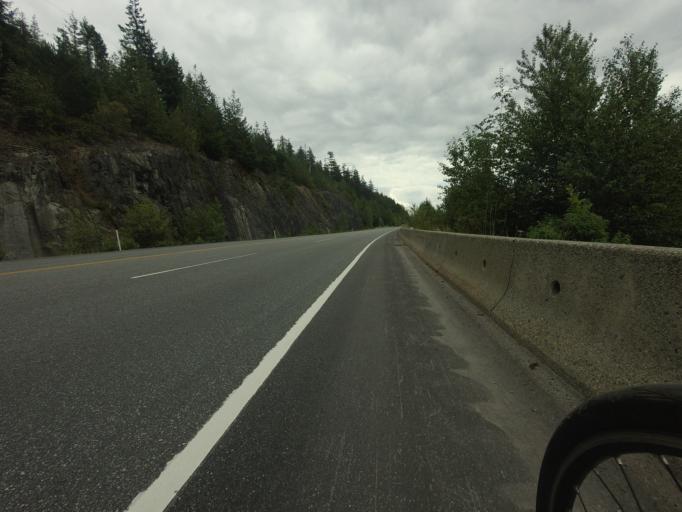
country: CA
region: British Columbia
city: Whistler
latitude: 49.8538
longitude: -123.1515
